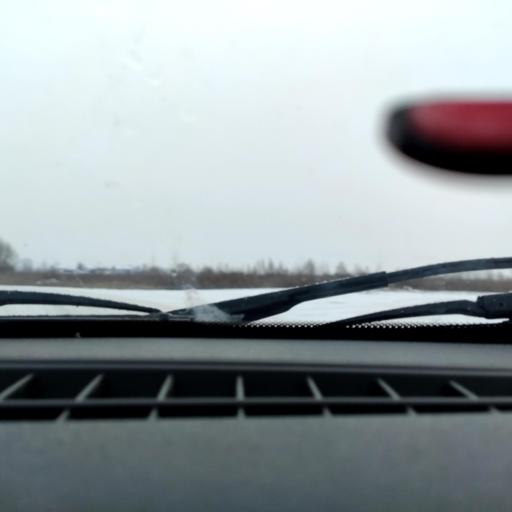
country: RU
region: Bashkortostan
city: Blagoveshchensk
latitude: 54.9059
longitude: 56.0096
